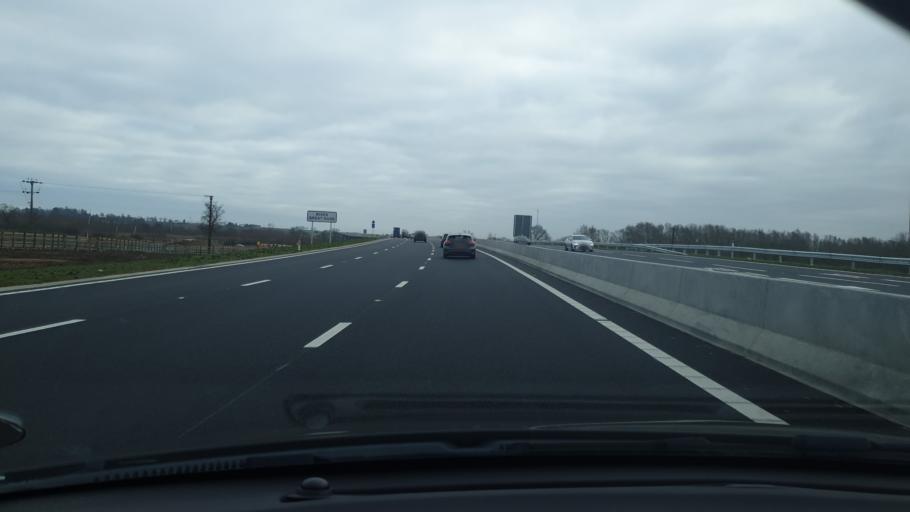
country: GB
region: England
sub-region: Cambridgeshire
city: Brampton
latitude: 52.3007
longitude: -0.2254
